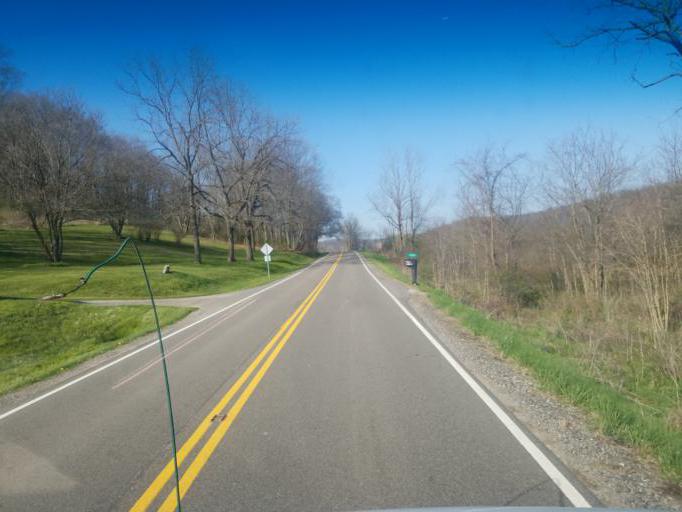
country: US
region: Ohio
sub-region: Knox County
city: Oak Hill
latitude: 40.3227
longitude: -82.0790
